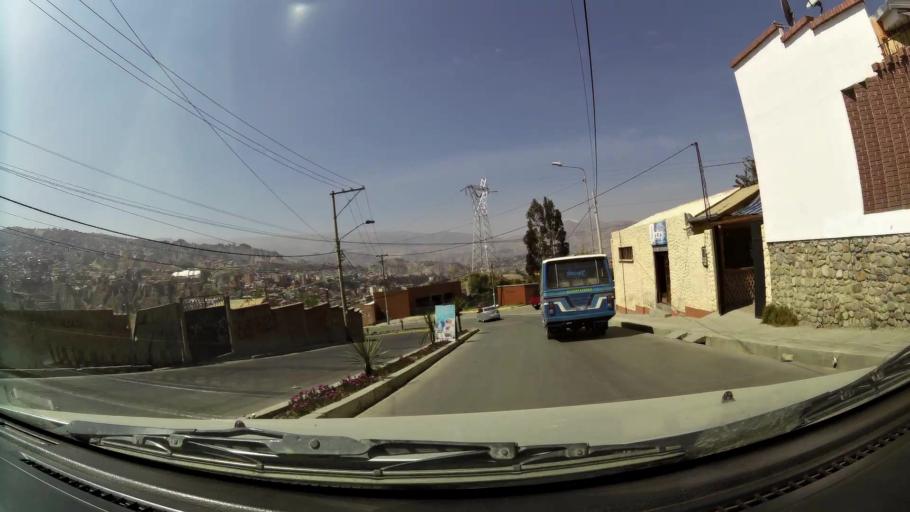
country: BO
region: La Paz
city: La Paz
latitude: -16.5227
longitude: -68.1204
